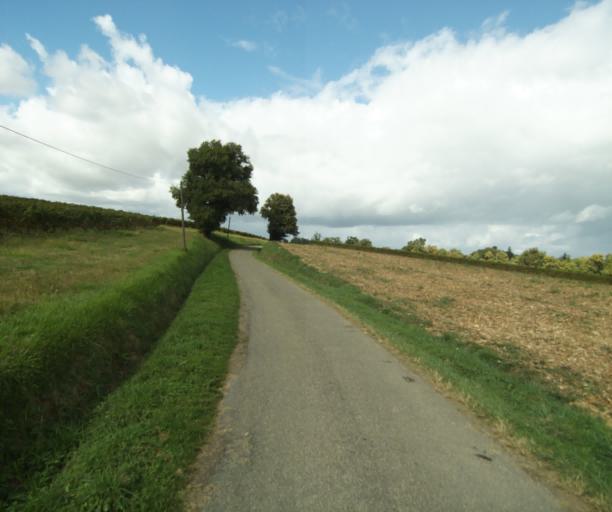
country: FR
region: Midi-Pyrenees
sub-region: Departement du Gers
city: Cazaubon
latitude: 43.8504
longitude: -0.0323
